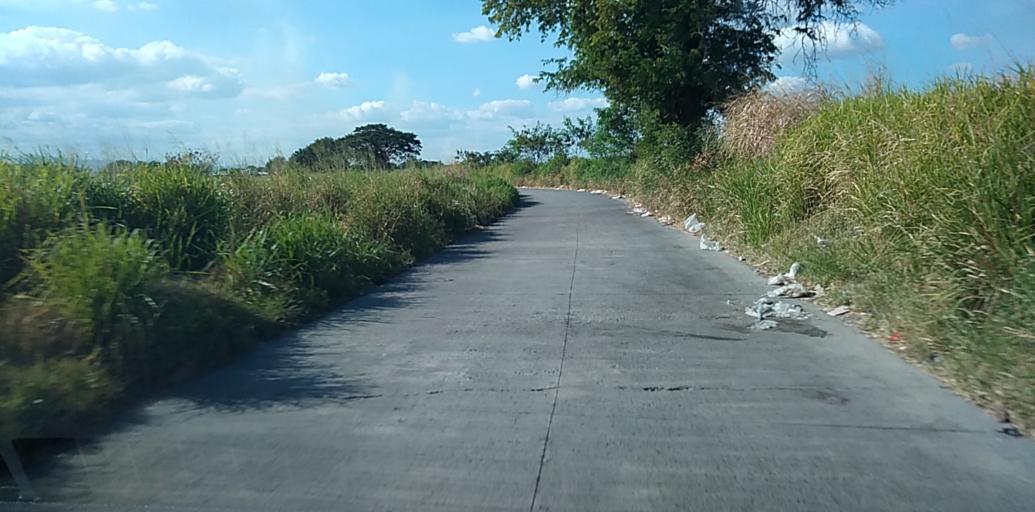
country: PH
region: Central Luzon
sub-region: Province of Pampanga
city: Acli
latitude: 15.1150
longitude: 120.6462
